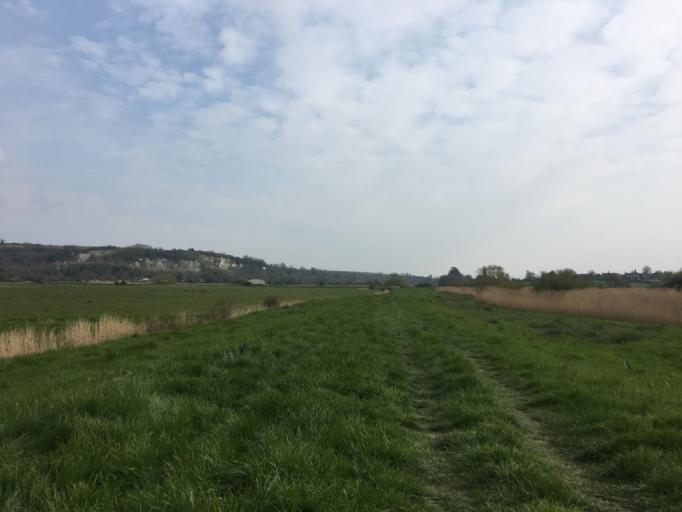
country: GB
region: England
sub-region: West Sussex
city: Arundel
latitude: 50.9021
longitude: -0.5532
